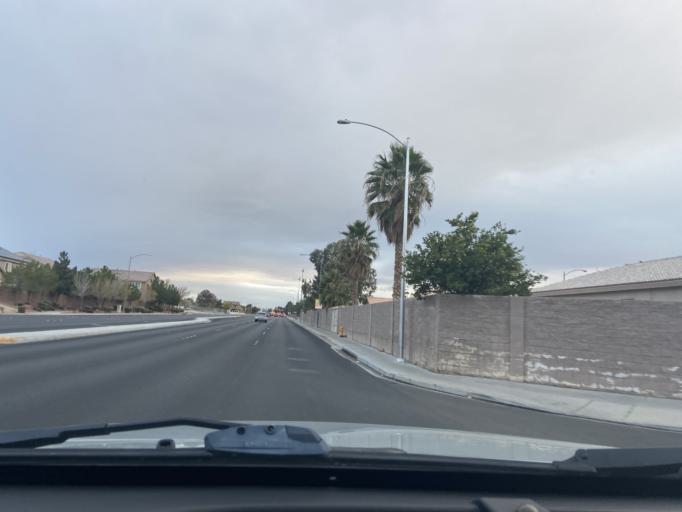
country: US
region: Nevada
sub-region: Clark County
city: North Las Vegas
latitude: 36.2372
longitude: -115.1803
